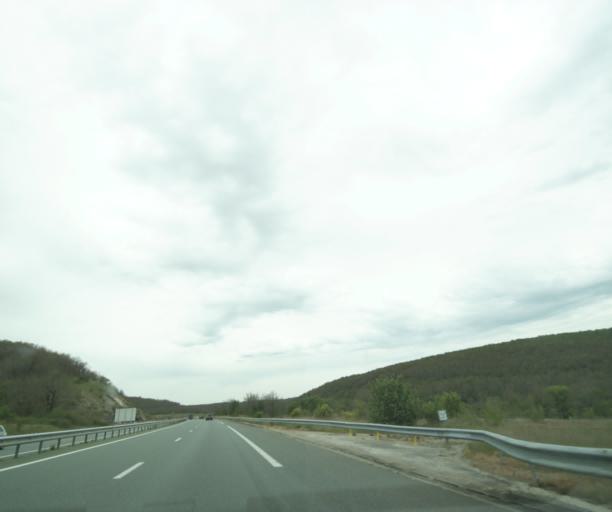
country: FR
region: Midi-Pyrenees
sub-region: Departement du Lot
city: Le Vigan
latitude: 44.7748
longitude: 1.5366
